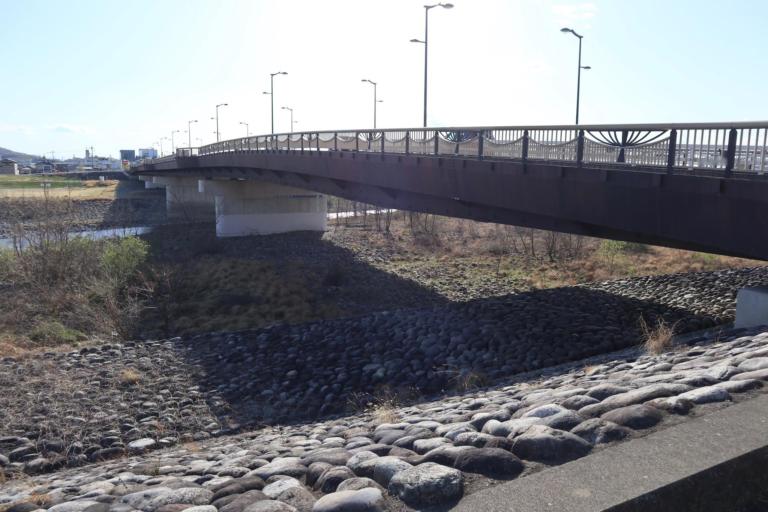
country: JP
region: Gunma
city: Kiryu
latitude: 36.4002
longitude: 139.3300
